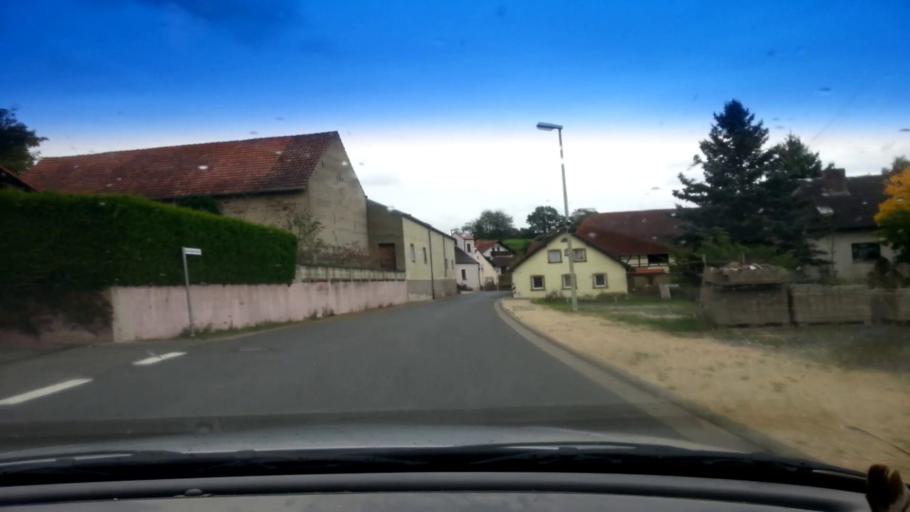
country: DE
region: Bavaria
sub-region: Upper Franconia
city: Lauter
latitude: 49.9908
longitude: 10.7573
